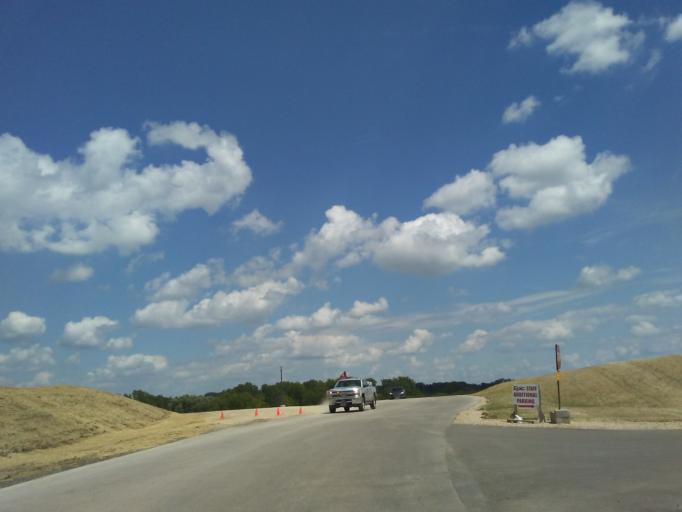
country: US
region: Wisconsin
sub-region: Dane County
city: Verona
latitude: 43.0029
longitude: -89.5668
